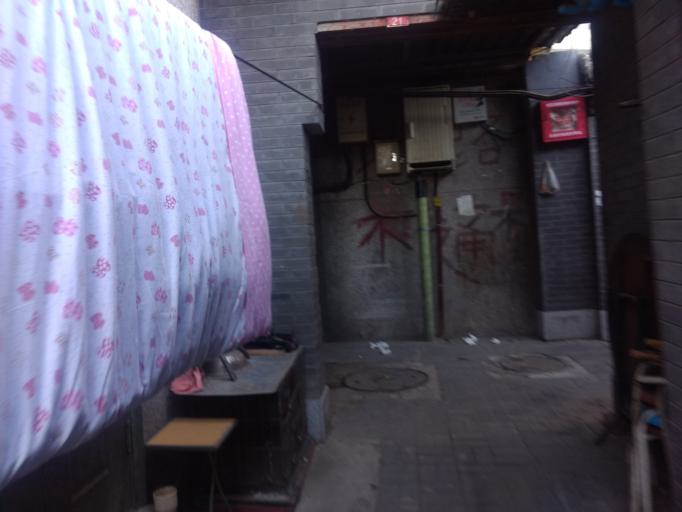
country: CN
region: Beijing
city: Beijing
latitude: 39.8889
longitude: 116.3813
